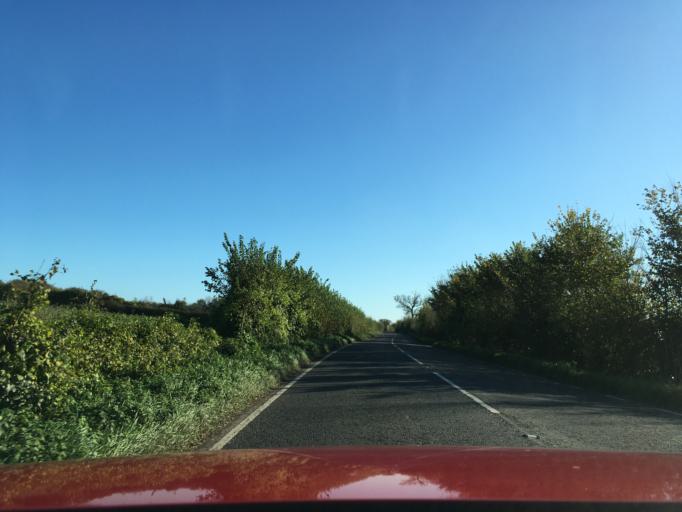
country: GB
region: England
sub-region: Somerset
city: Langport
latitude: 51.0352
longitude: -2.7821
